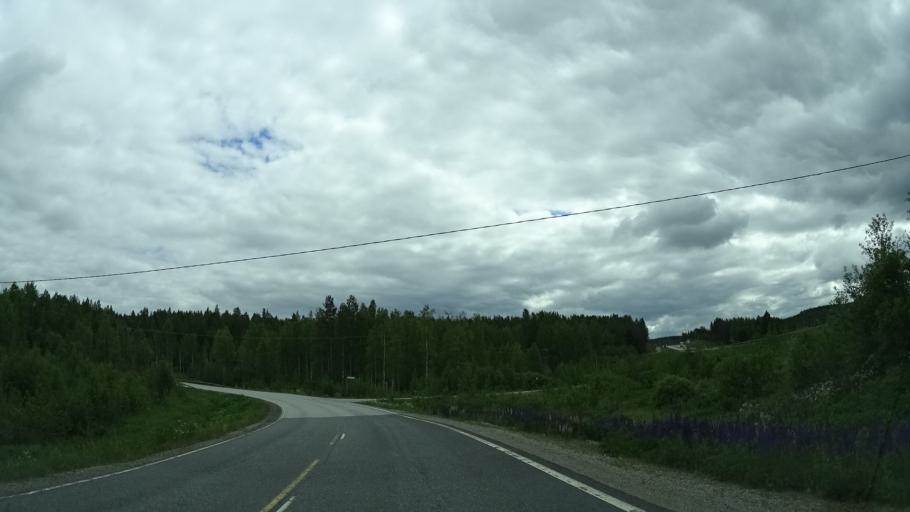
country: FI
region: Central Finland
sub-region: Jyvaeskylae
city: Toivakka
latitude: 62.0779
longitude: 26.0358
